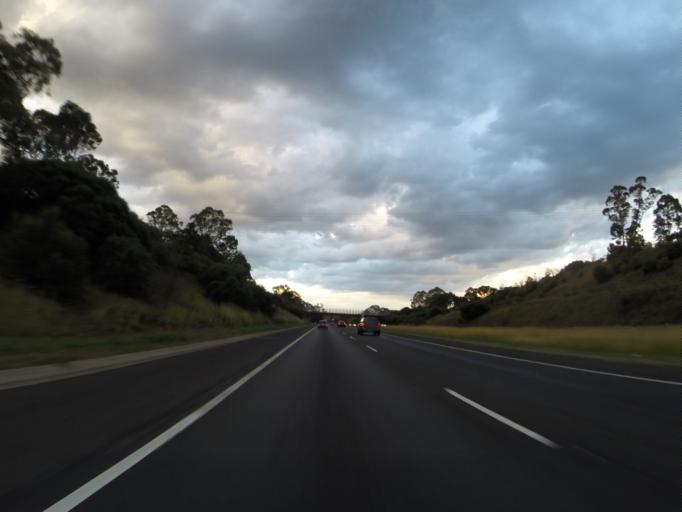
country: AU
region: New South Wales
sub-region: Campbelltown Municipality
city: Glen Alpine
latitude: -34.1084
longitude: 150.7613
